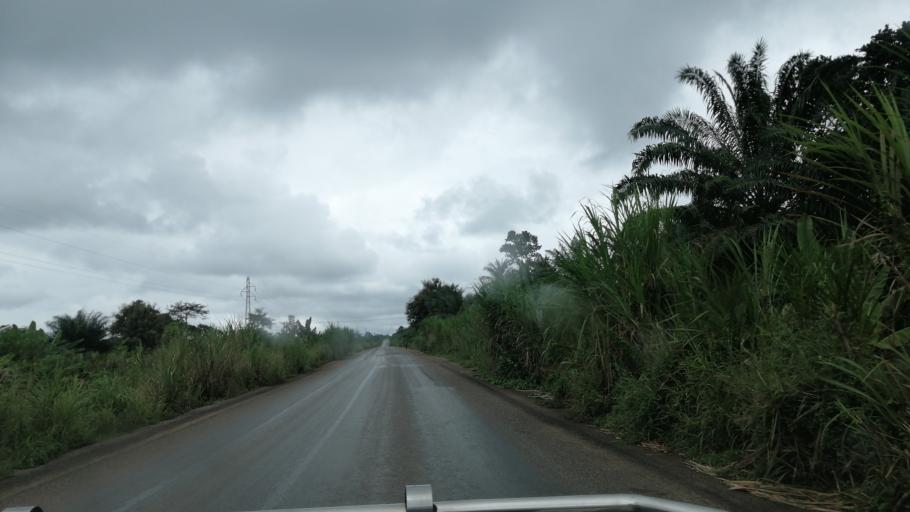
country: GH
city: Duayaw Nkwanta
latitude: 6.9011
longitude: -2.4017
